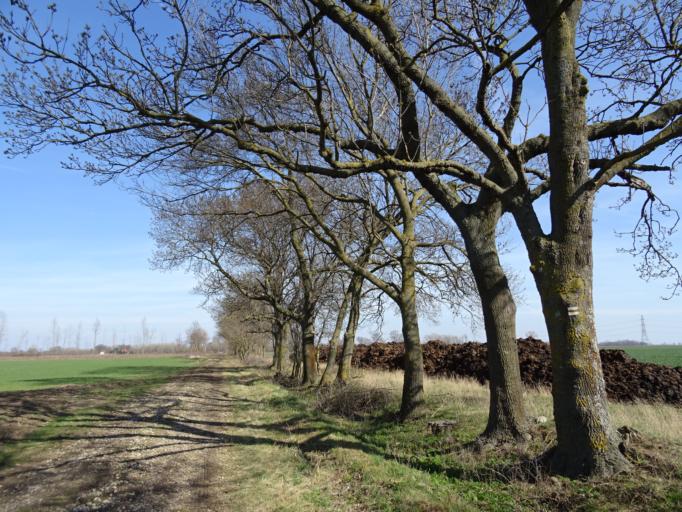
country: HU
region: Gyor-Moson-Sopron
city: Farad
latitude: 47.5456
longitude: 17.1670
